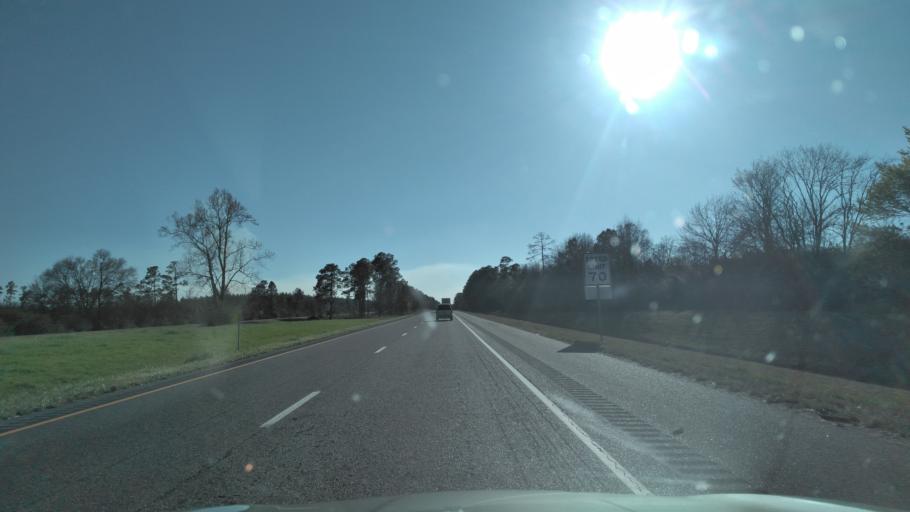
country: US
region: Alabama
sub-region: Escambia County
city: Atmore
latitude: 31.0767
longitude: -87.5453
